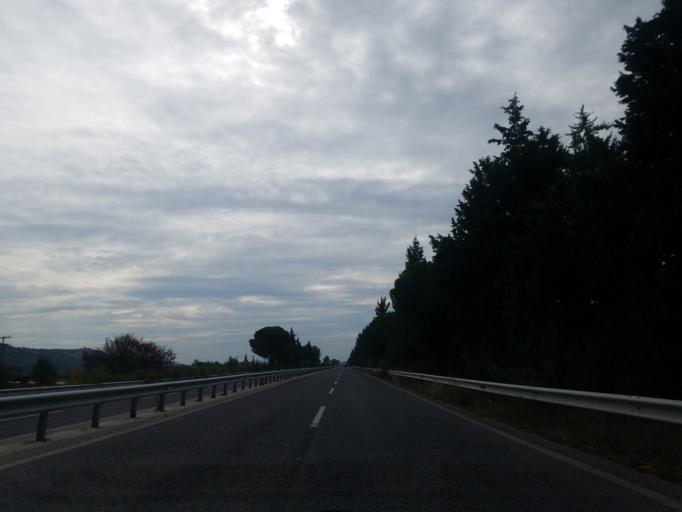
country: GR
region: Thessaly
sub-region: Trikala
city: Vasiliki
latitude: 39.6467
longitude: 21.6880
